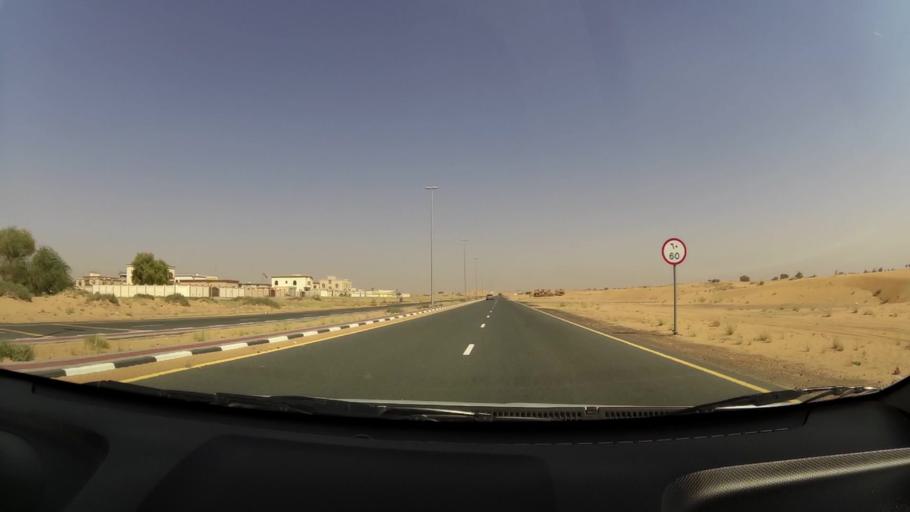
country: AE
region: Umm al Qaywayn
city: Umm al Qaywayn
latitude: 25.4717
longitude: 55.6107
